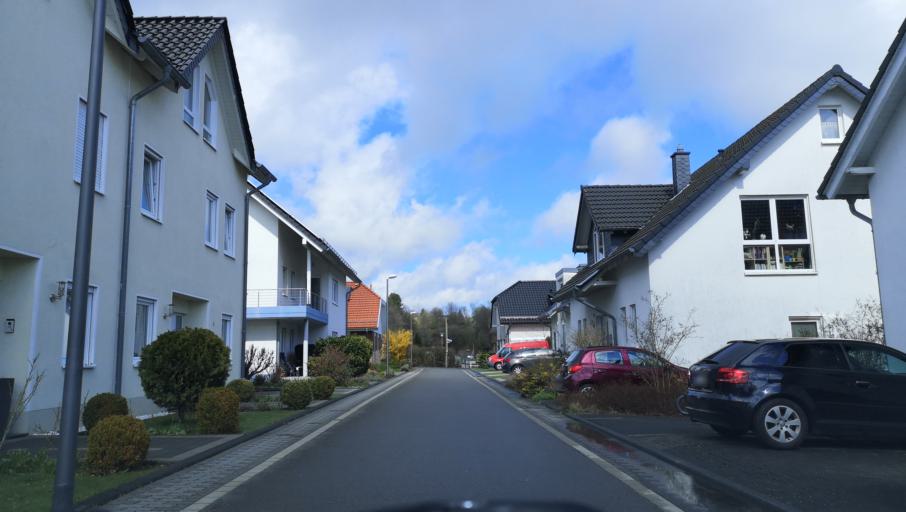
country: DE
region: North Rhine-Westphalia
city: Radevormwald
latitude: 51.1967
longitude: 7.3664
